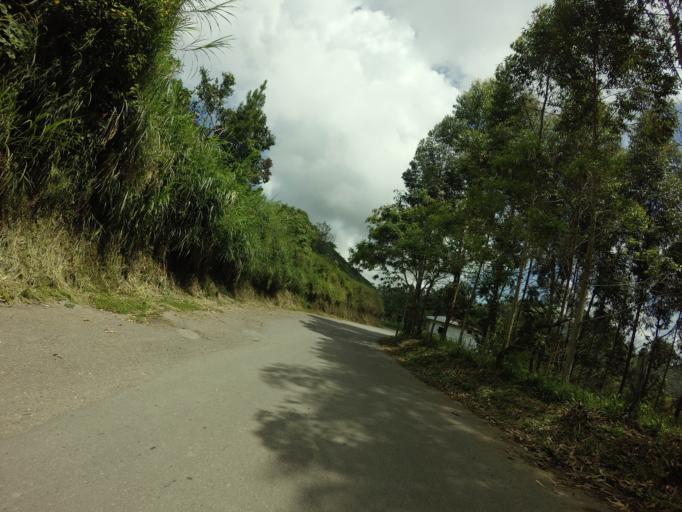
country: CO
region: Caldas
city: Marquetalia
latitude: 5.2976
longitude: -75.0451
